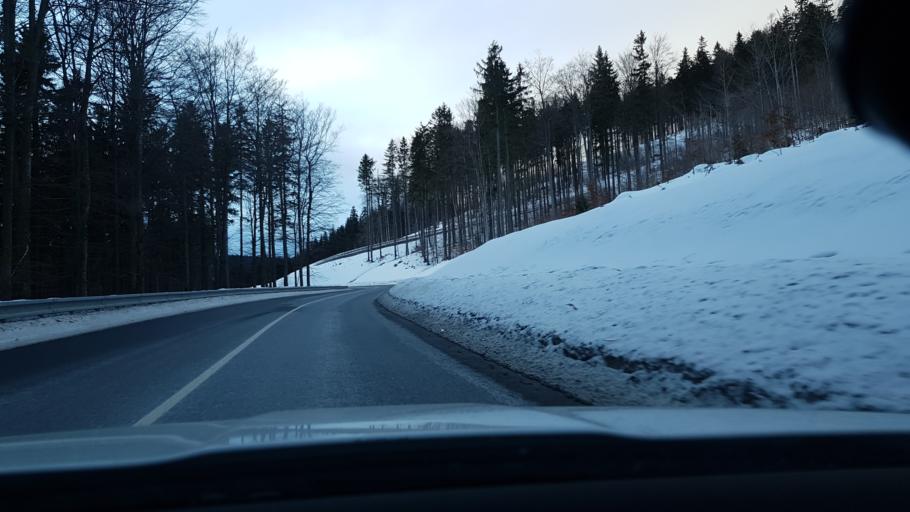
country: CZ
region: Olomoucky
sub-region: Okres Sumperk
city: Loucna nad Desnou
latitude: 50.1131
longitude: 17.1497
